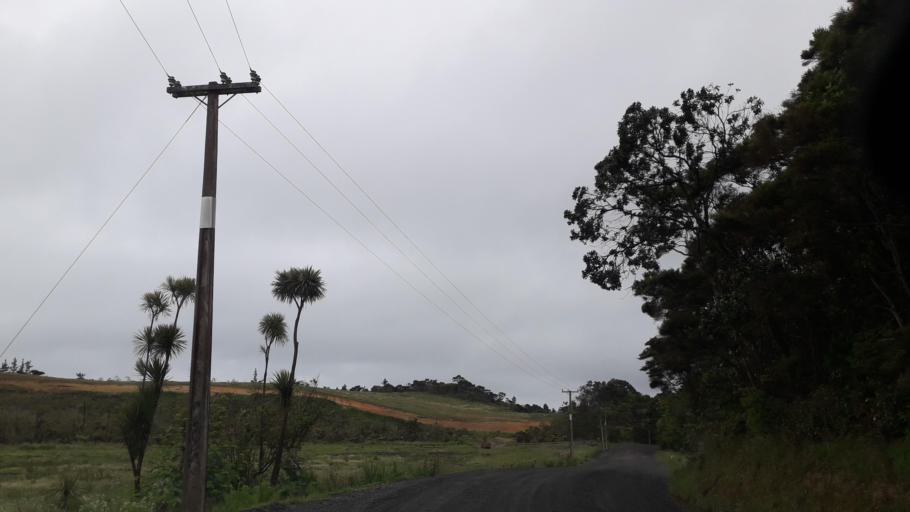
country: NZ
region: Northland
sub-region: Far North District
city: Paihia
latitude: -35.2397
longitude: 174.2482
